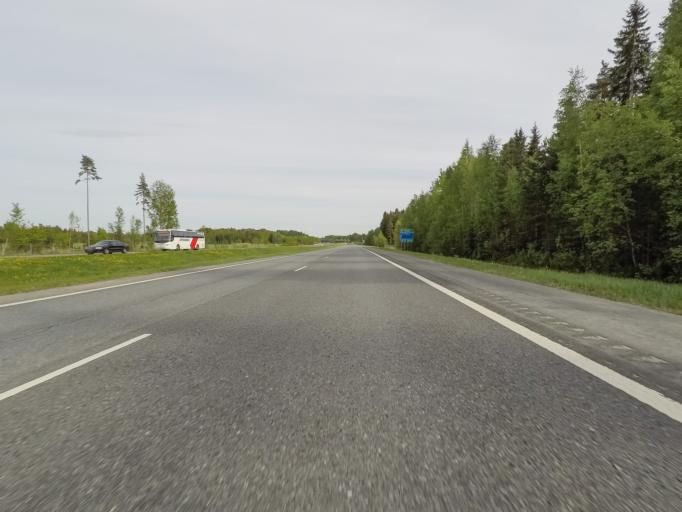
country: FI
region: Haeme
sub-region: Haemeenlinna
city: Kalvola
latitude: 61.1037
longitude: 24.1529
